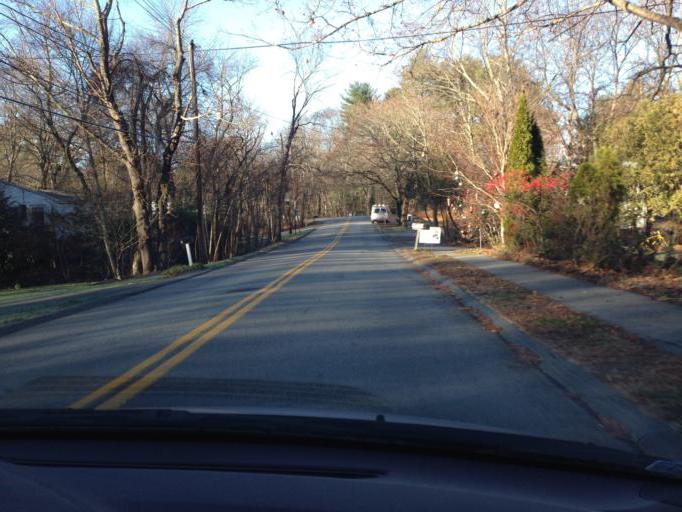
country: US
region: Massachusetts
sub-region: Middlesex County
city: Bedford
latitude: 42.5137
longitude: -71.2829
